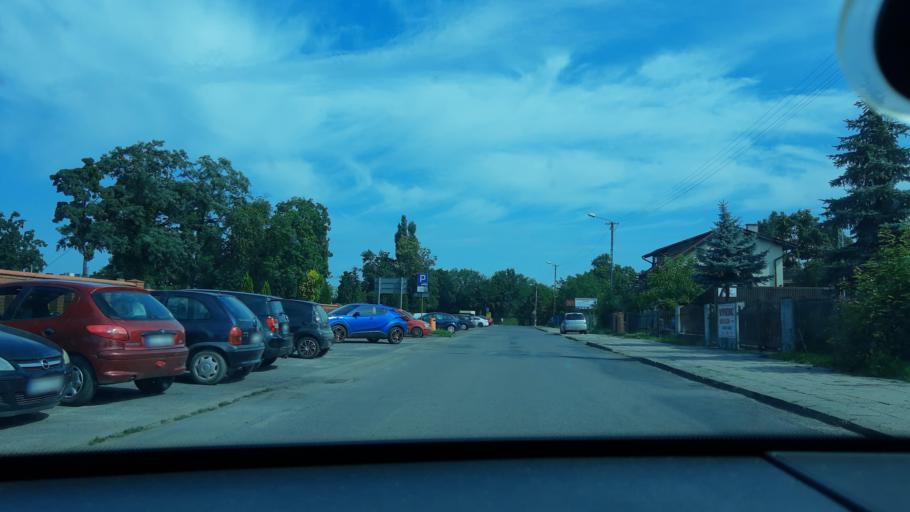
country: PL
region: Lodz Voivodeship
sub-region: Powiat sieradzki
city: Sieradz
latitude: 51.5982
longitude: 18.7280
